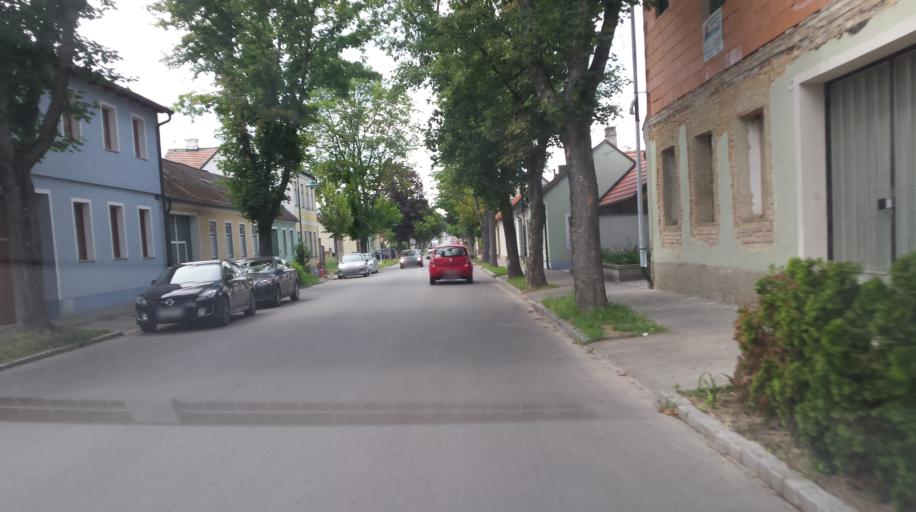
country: AT
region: Lower Austria
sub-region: Politischer Bezirk Mistelbach
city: Wolkersdorf im Weinviertel
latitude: 48.3737
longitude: 16.5207
